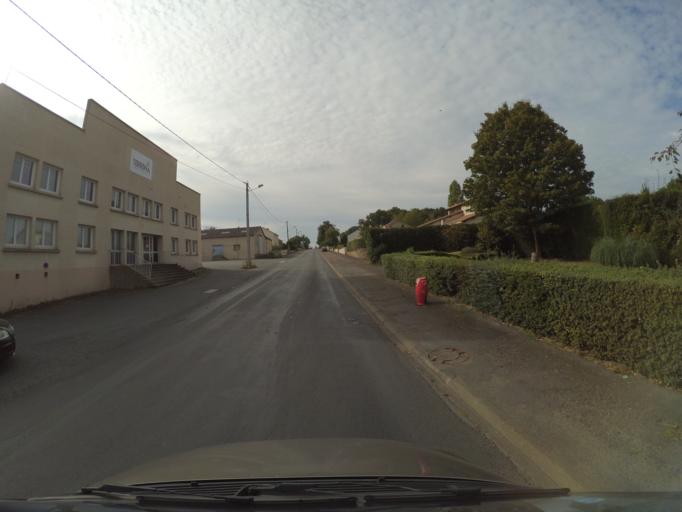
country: FR
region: Pays de la Loire
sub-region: Departement de Maine-et-Loire
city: Villedieu-la-Blouere
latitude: 47.1554
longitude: -1.0558
